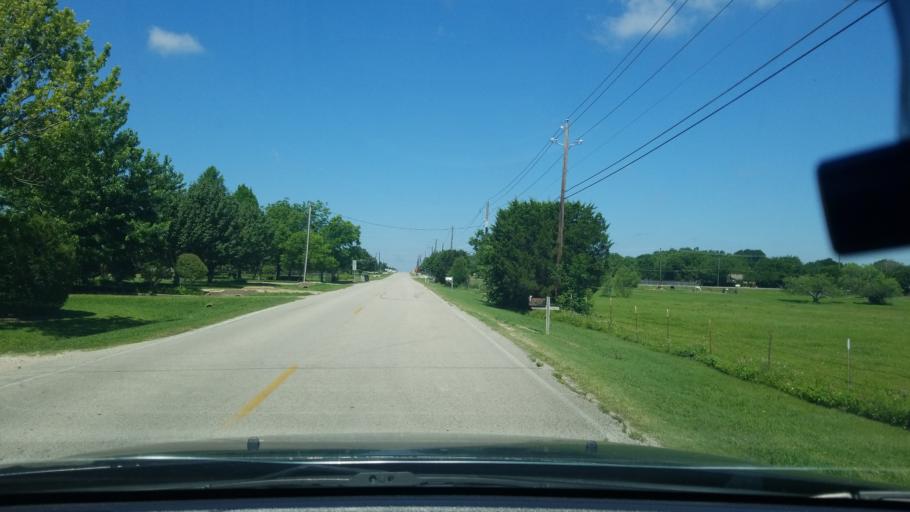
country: US
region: Texas
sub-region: Dallas County
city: Sunnyvale
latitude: 32.7961
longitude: -96.5760
